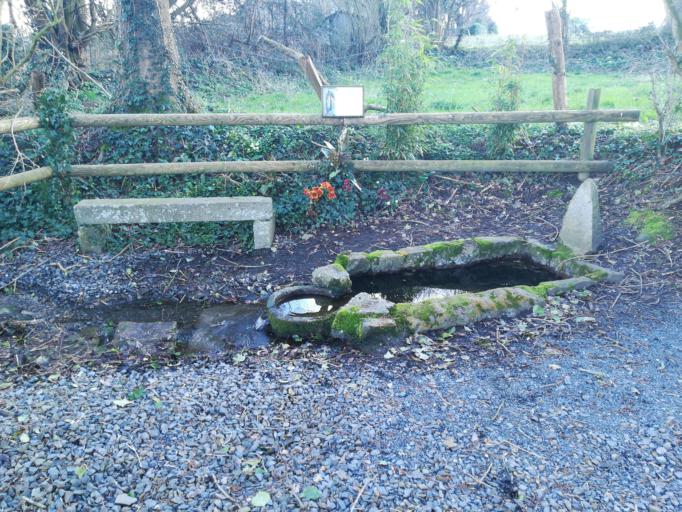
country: FR
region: Lower Normandy
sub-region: Departement de la Manche
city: Saint-Quentin-sur-le-Homme
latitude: 48.6320
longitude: -1.3163
